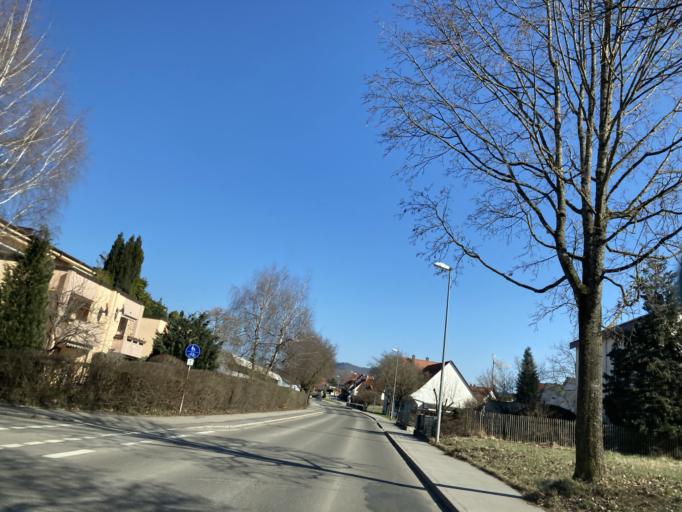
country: DE
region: Baden-Wuerttemberg
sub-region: Tuebingen Region
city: Bodelshausen
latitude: 48.3858
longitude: 8.9835
